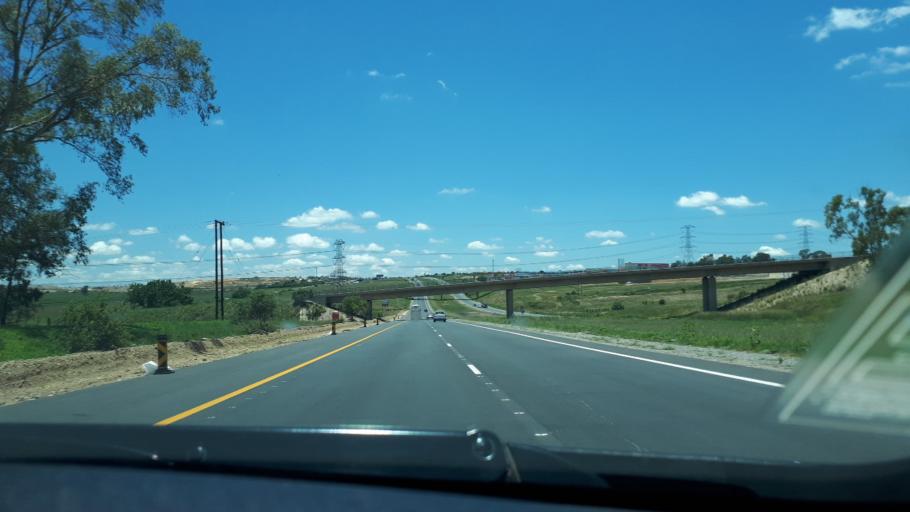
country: ZA
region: Gauteng
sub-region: City of Johannesburg Metropolitan Municipality
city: Diepsloot
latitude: -25.9328
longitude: 27.9871
